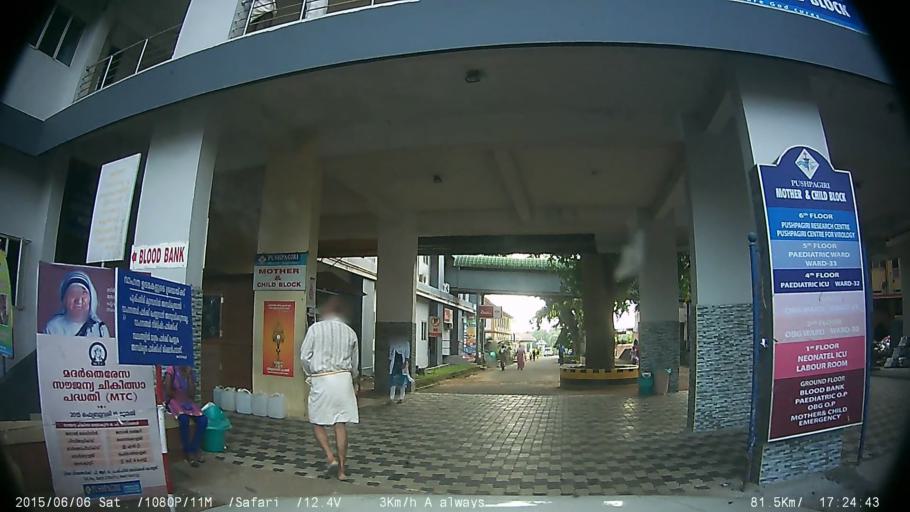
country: IN
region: Kerala
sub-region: Pattanamtitta
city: Tiruvalla
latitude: 9.3807
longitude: 76.5808
